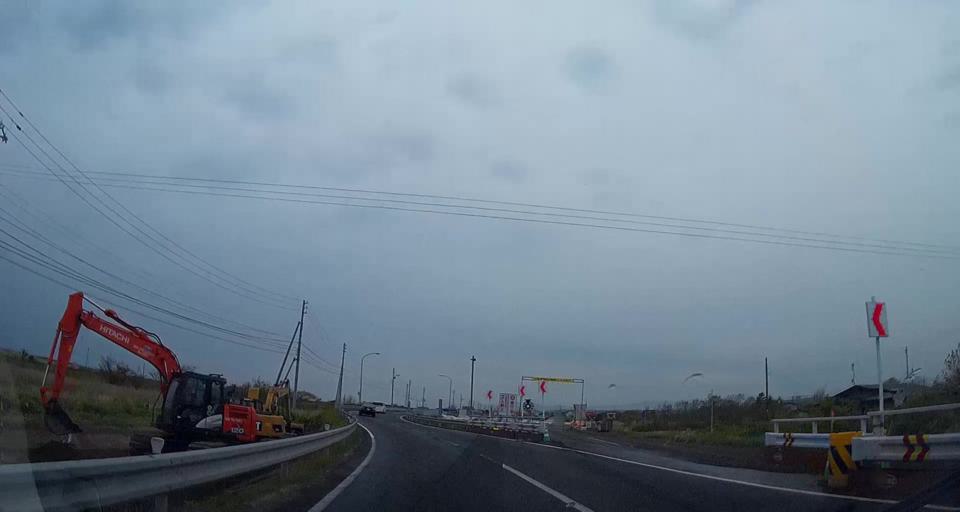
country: JP
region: Hokkaido
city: Shiraoi
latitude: 42.5799
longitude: 141.4238
